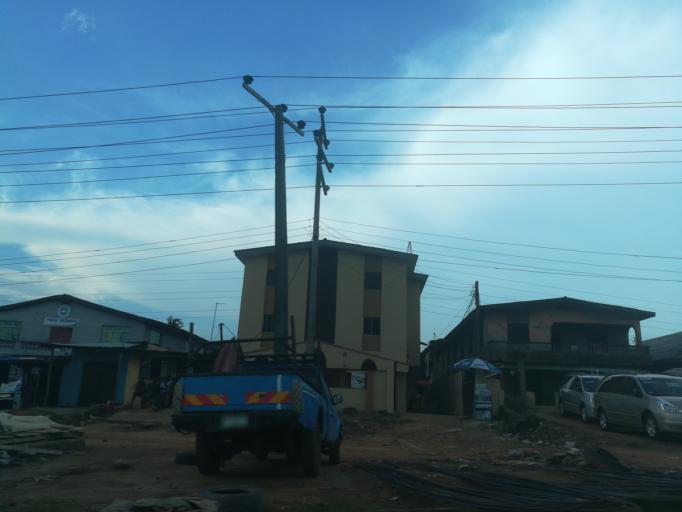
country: NG
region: Lagos
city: Ikorodu
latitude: 6.6251
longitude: 3.4907
